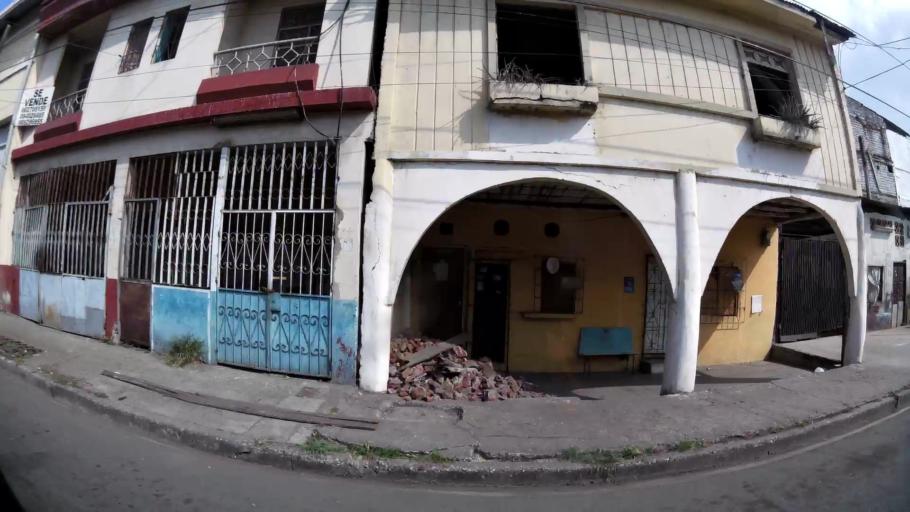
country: EC
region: Guayas
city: Guayaquil
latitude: -2.2151
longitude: -79.9051
